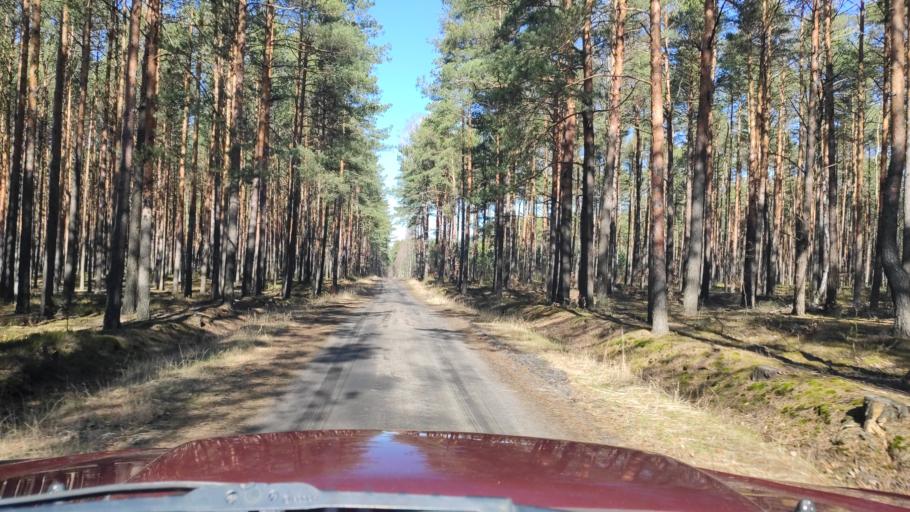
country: PL
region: Masovian Voivodeship
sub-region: Powiat zwolenski
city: Zwolen
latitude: 51.4274
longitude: 21.5496
